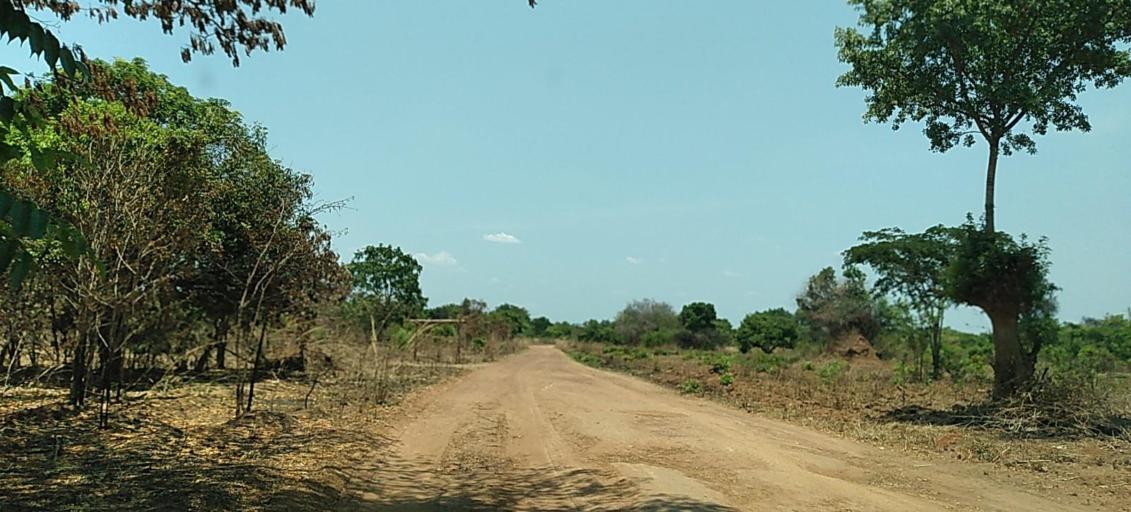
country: ZM
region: Copperbelt
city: Luanshya
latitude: -13.0974
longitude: 28.4056
